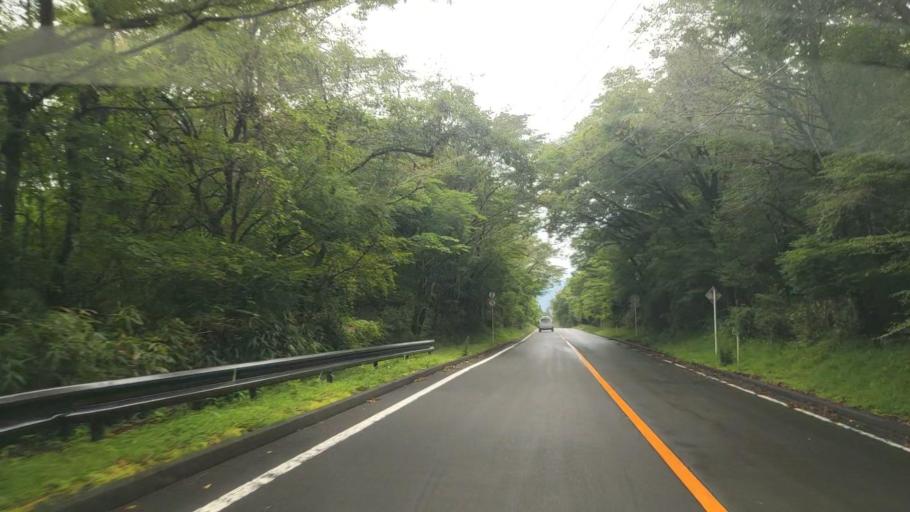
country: JP
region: Shizuoka
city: Gotemba
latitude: 35.2824
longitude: 138.7931
